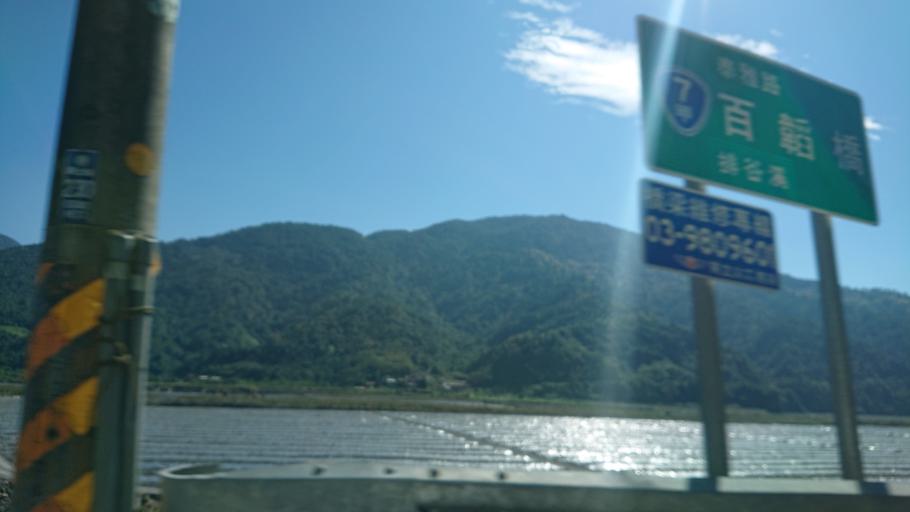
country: TW
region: Taiwan
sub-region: Yilan
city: Yilan
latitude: 24.5971
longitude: 121.5129
